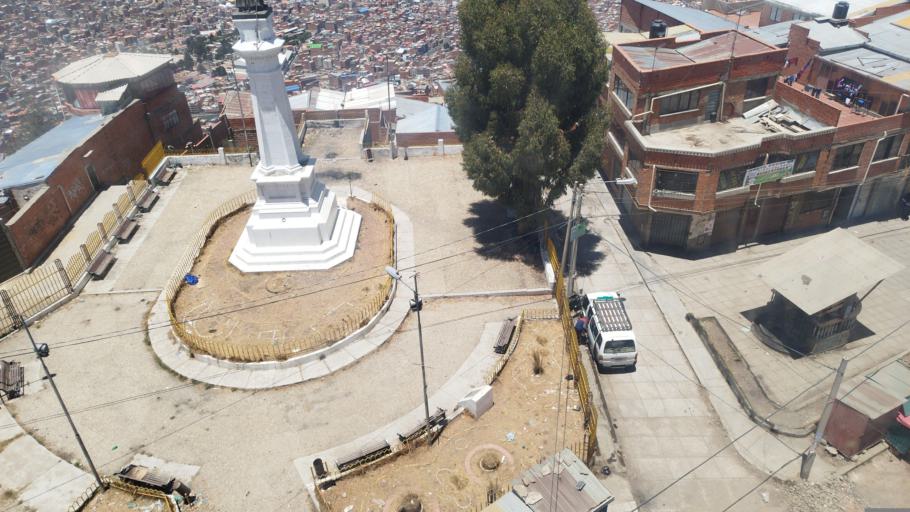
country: BO
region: La Paz
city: La Paz
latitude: -16.5053
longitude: -68.1593
